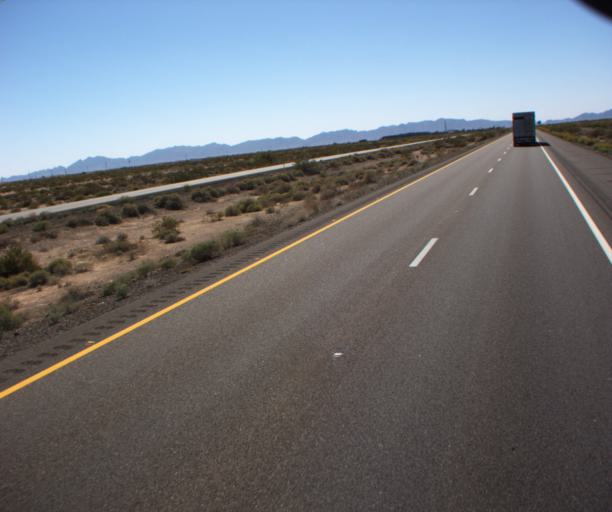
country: US
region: Arizona
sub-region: Yuma County
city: Wellton
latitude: 32.8085
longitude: -113.5207
